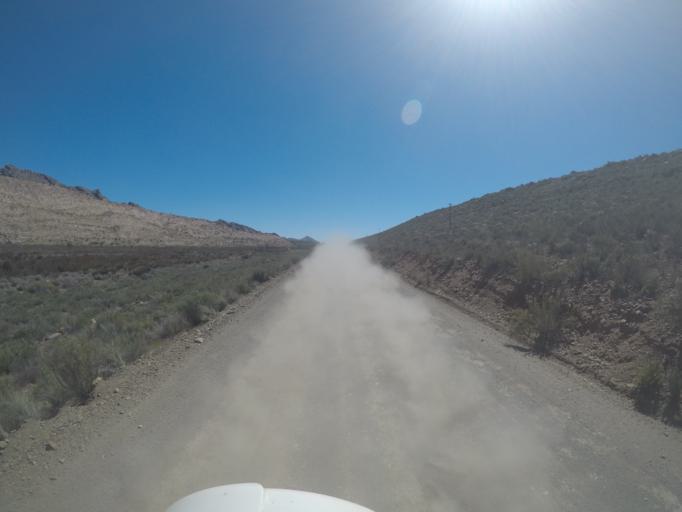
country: ZA
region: Western Cape
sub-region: Cape Winelands District Municipality
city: Ceres
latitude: -32.8228
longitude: 19.4534
